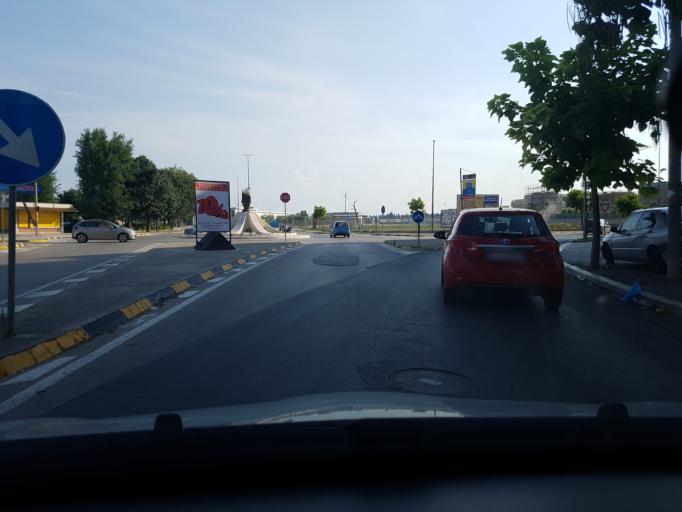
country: IT
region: Apulia
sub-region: Provincia di Foggia
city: Cerignola
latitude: 41.2608
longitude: 15.9075
